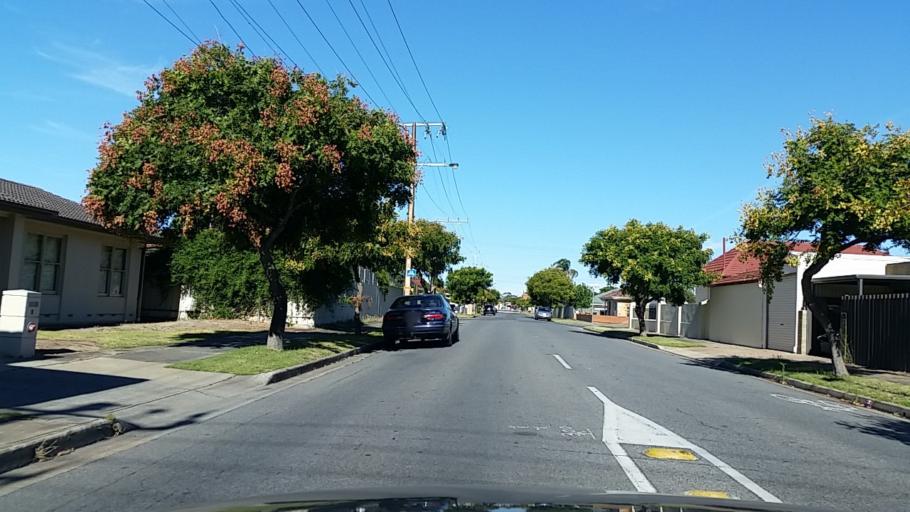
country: AU
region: South Australia
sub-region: Charles Sturt
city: Royal Park
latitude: -34.8695
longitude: 138.5079
